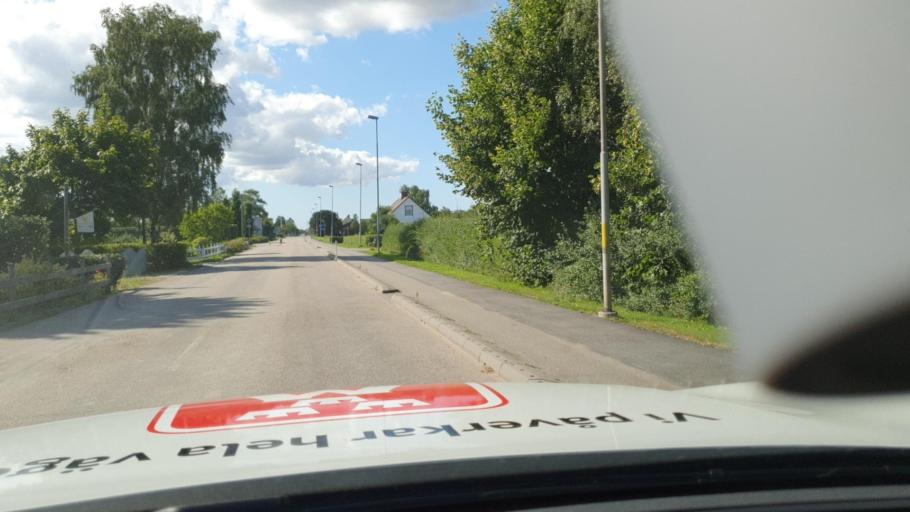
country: SE
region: Skane
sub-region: Astorps Kommun
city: Kvidinge
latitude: 56.1308
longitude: 13.0671
